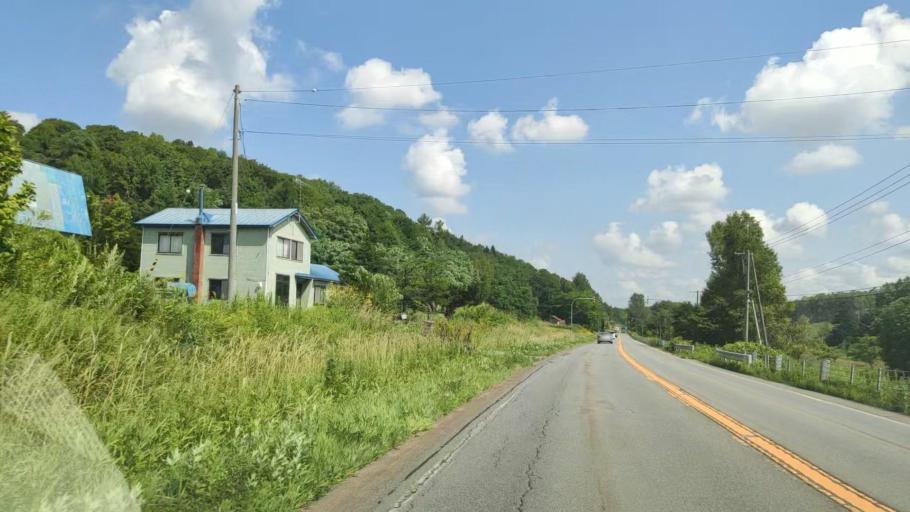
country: JP
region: Hokkaido
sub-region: Asahikawa-shi
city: Asahikawa
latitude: 43.5671
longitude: 142.4352
